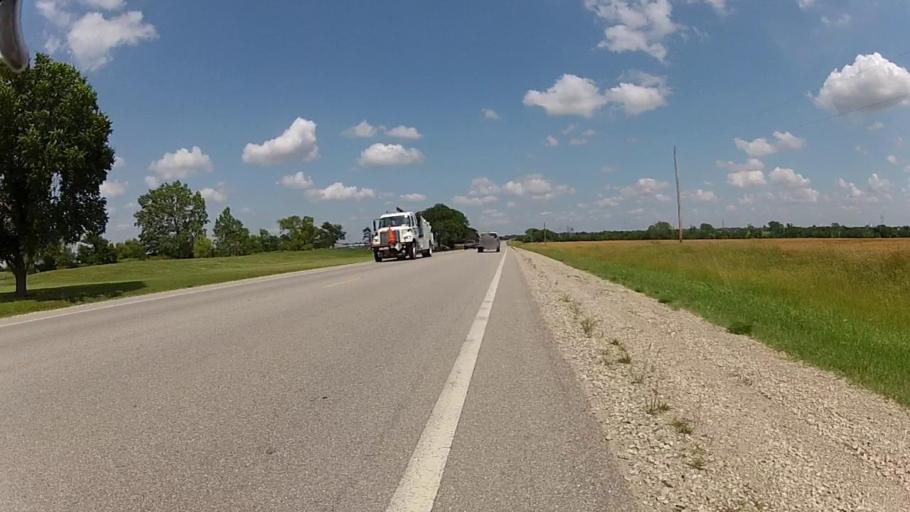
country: US
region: Kansas
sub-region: Labette County
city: Oswego
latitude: 37.1934
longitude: -95.1574
